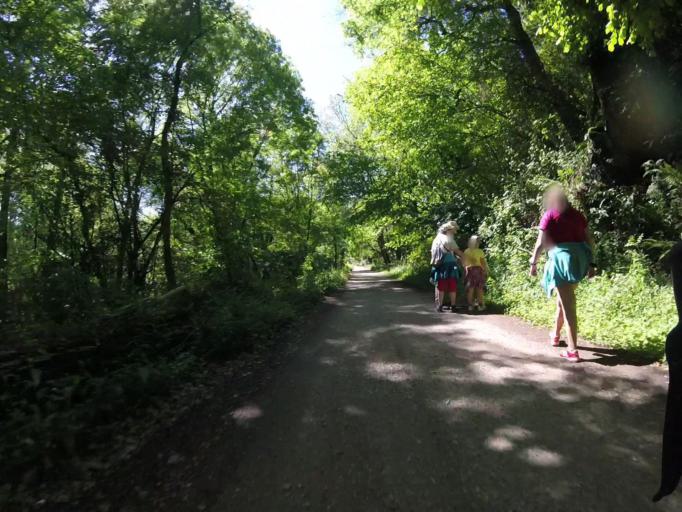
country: ES
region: Navarre
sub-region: Provincia de Navarra
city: Bera
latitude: 43.2780
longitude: -1.7135
